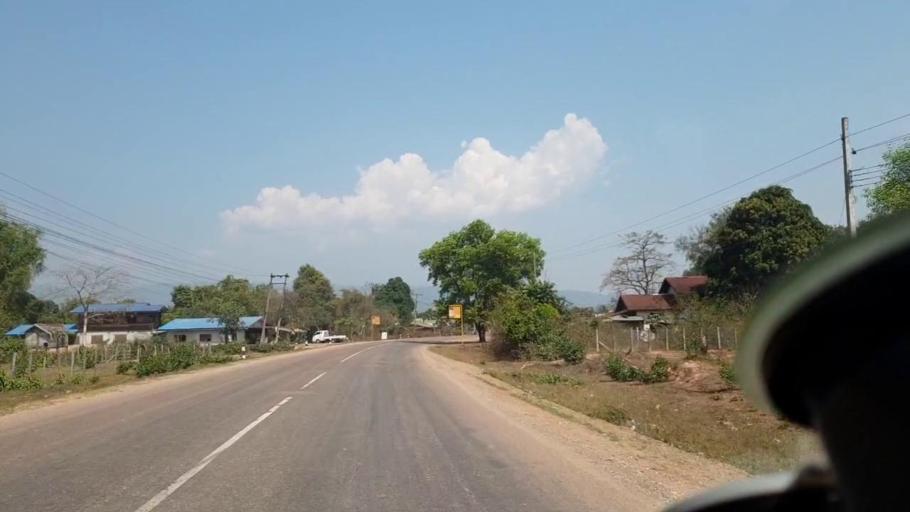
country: TH
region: Nong Khai
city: Rattanawapi
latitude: 18.1674
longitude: 103.0555
